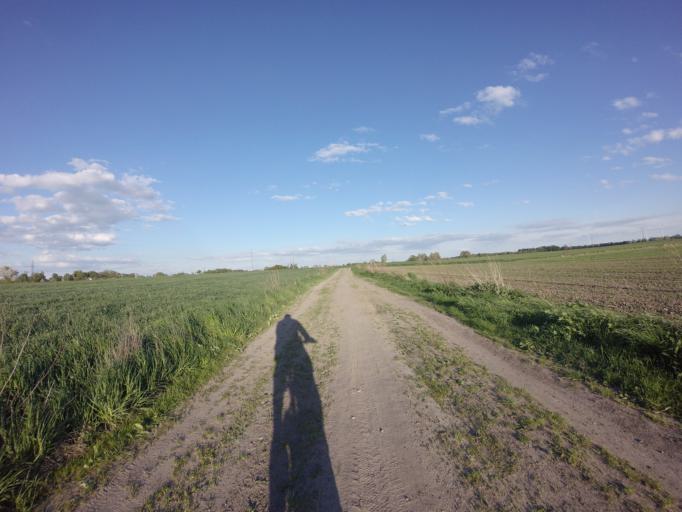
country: PL
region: West Pomeranian Voivodeship
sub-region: Powiat choszczenski
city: Choszczno
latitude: 53.1441
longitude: 15.4238
